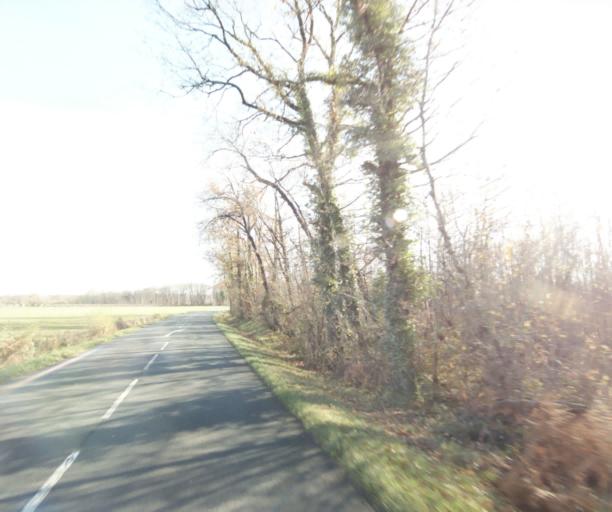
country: FR
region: Poitou-Charentes
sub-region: Departement de la Charente-Maritime
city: Ecoyeux
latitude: 45.7661
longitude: -0.5082
